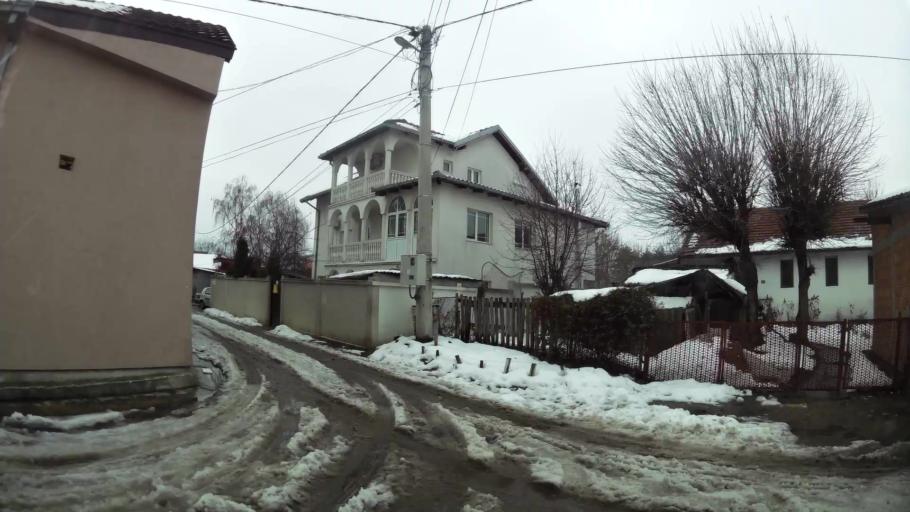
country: RS
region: Central Serbia
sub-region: Belgrade
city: Zemun
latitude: 44.8334
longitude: 20.3763
